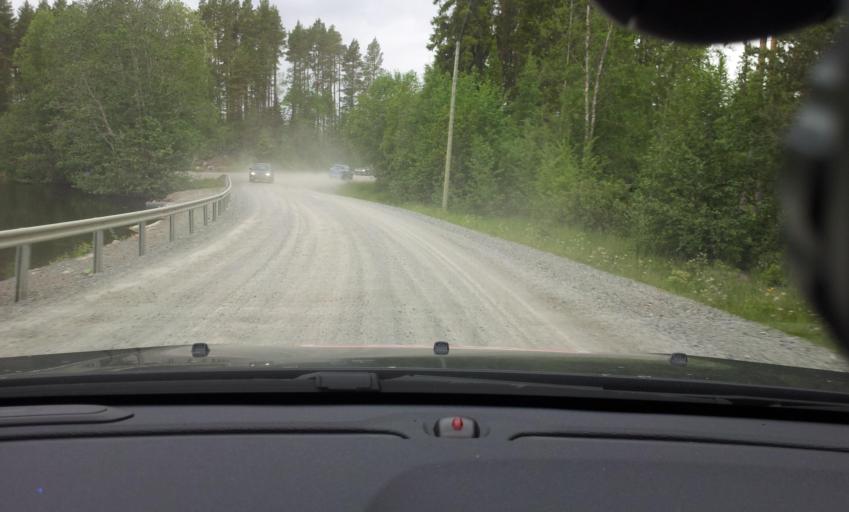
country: SE
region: Jaemtland
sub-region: OEstersunds Kommun
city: Ostersund
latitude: 62.9808
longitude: 14.6245
